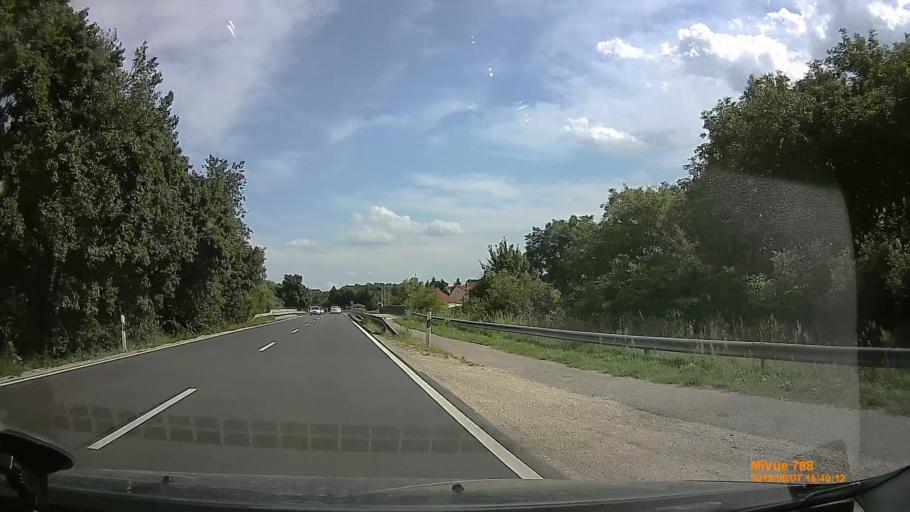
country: HU
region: Vas
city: Jak
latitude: 47.1522
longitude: 16.6400
